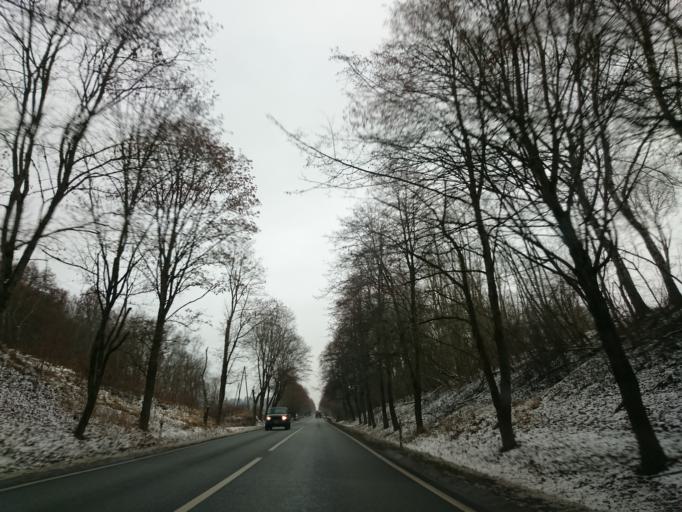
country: LV
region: Krimulda
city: Ragana
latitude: 57.1523
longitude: 24.6844
